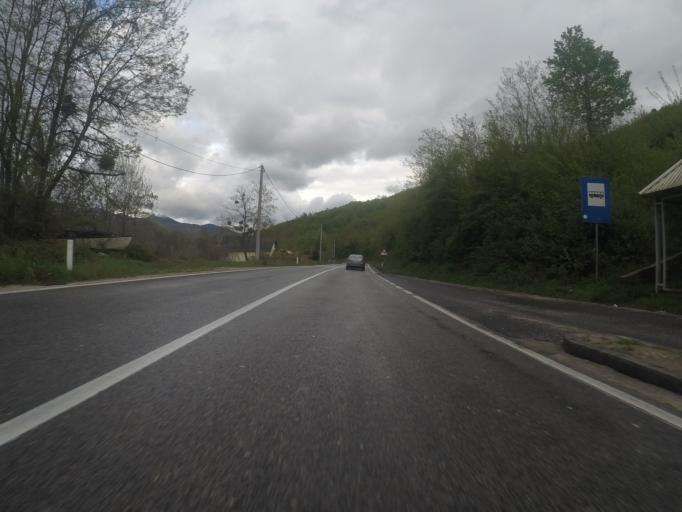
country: BA
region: Federation of Bosnia and Herzegovina
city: Jablanica
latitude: 43.6931
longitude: 17.8520
